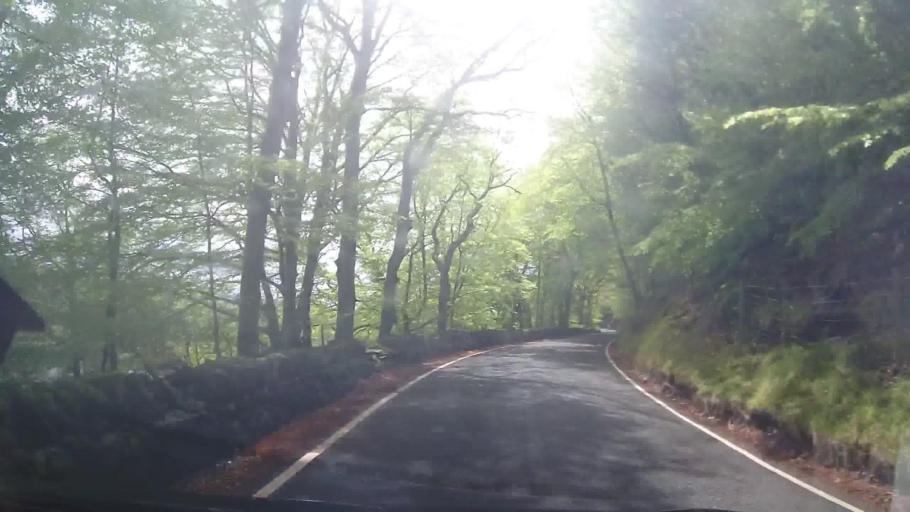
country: GB
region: Wales
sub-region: Gwynedd
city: Penrhyndeudraeth
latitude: 52.9710
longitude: -4.0969
